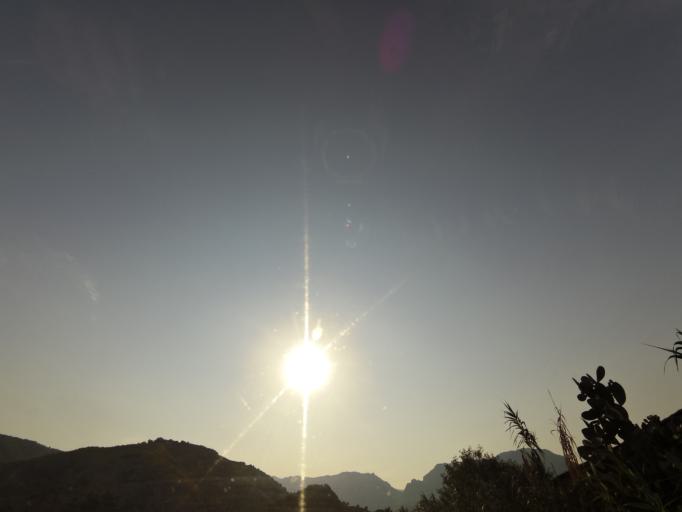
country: IT
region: Calabria
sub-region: Provincia di Reggio Calabria
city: Stilo
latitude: 38.4644
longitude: 16.4994
